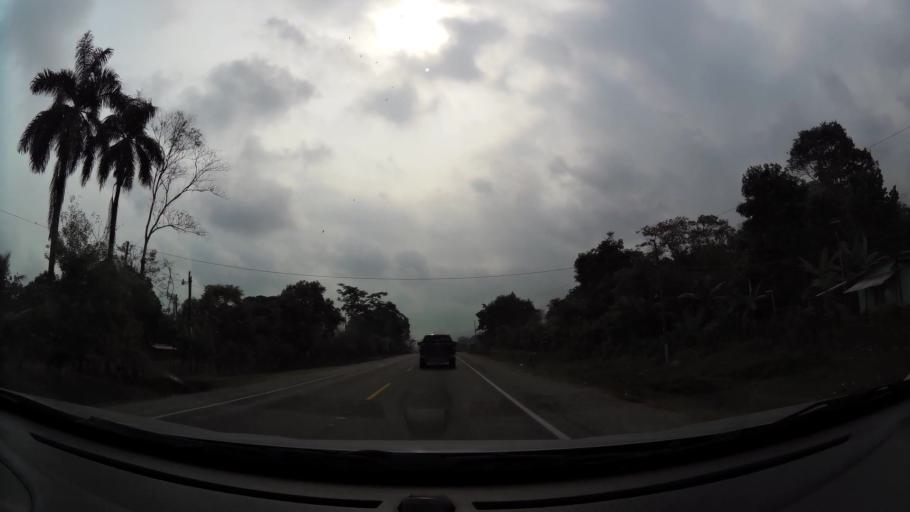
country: HN
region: Yoro
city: Guaimitas
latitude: 15.4934
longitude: -87.7428
